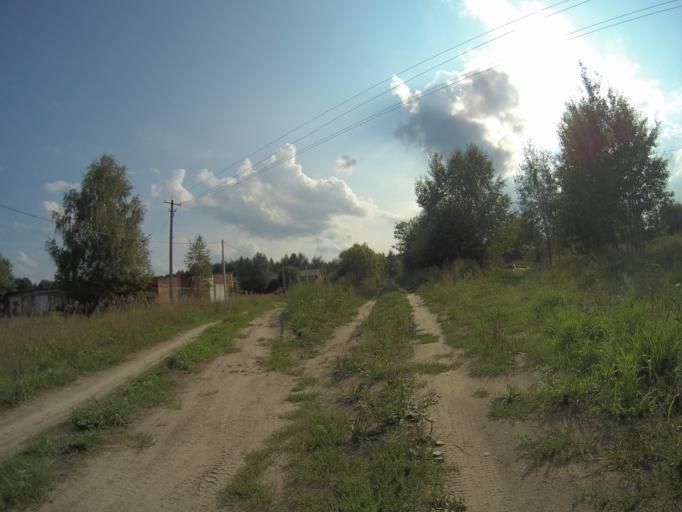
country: RU
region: Vladimir
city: Raduzhnyy
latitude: 56.0259
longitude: 40.3094
